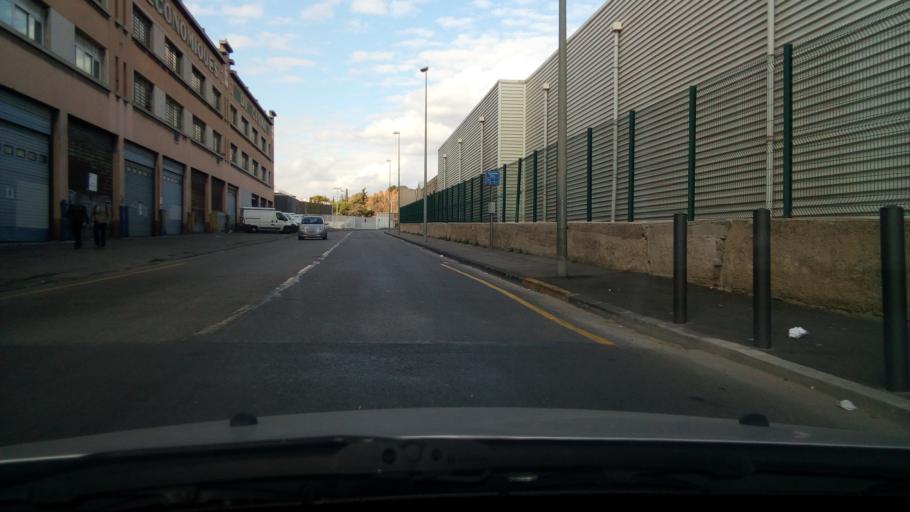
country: FR
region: Provence-Alpes-Cote d'Azur
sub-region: Departement des Bouches-du-Rhone
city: Marseille 14
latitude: 43.3297
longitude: 5.3672
